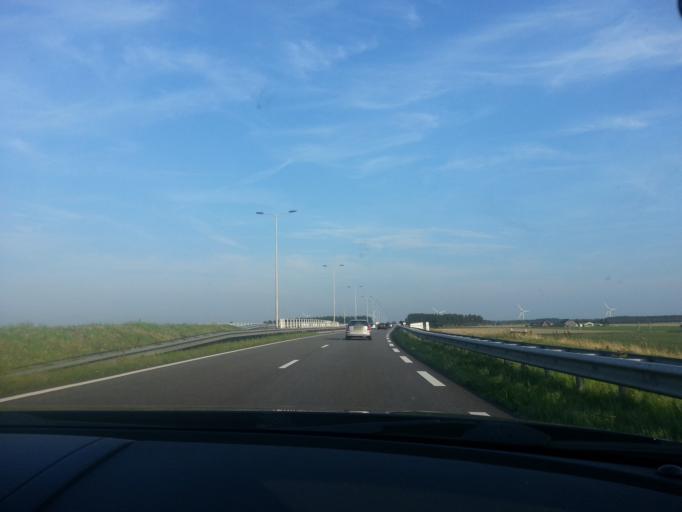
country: NL
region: South Holland
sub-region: Gemeente Kaag en Braassem
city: Oude Wetering
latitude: 52.2511
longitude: 4.6322
